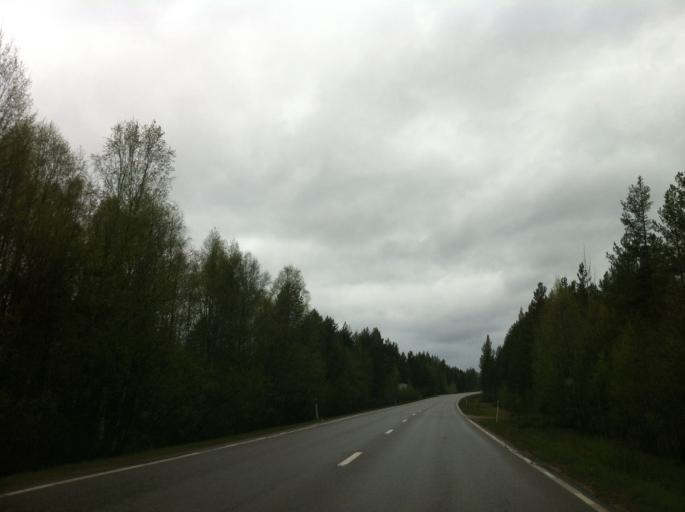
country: SE
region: Jaemtland
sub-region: Harjedalens Kommun
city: Sveg
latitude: 62.0467
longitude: 14.3356
